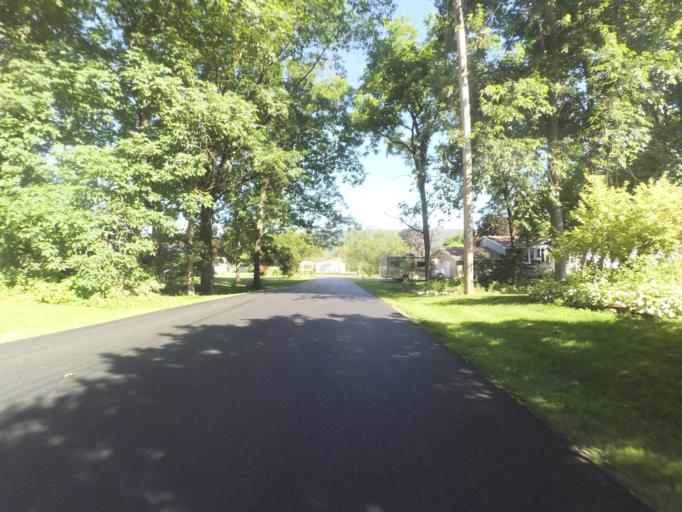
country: US
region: Pennsylvania
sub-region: Centre County
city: Centre Hall
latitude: 40.8352
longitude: -77.6772
